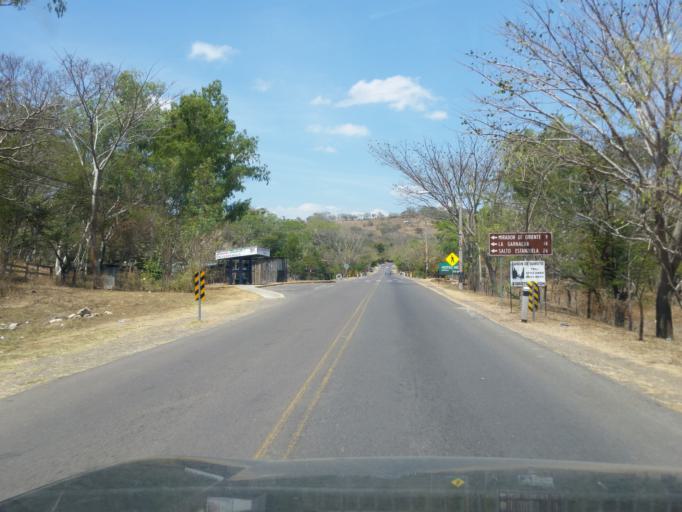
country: NI
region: Esteli
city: Esteli
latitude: 12.9999
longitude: -86.3042
